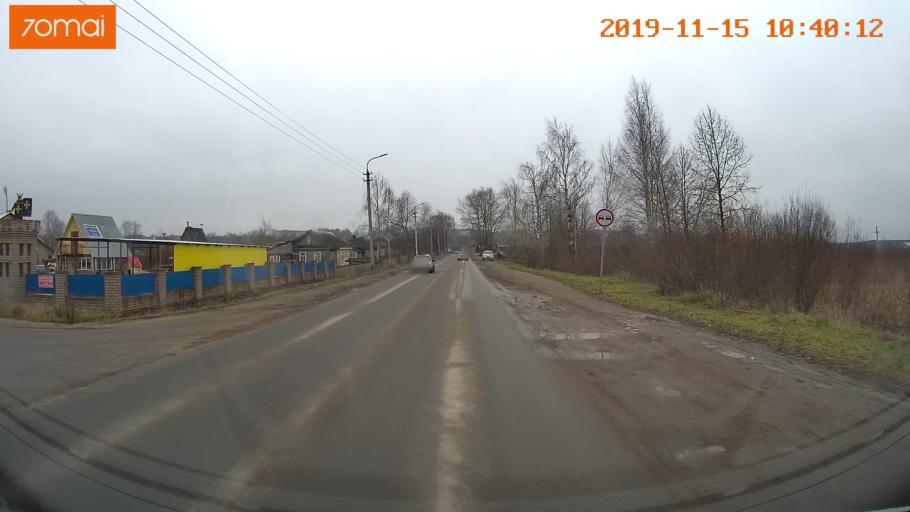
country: RU
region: Vologda
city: Sheksna
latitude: 59.2159
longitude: 38.5098
